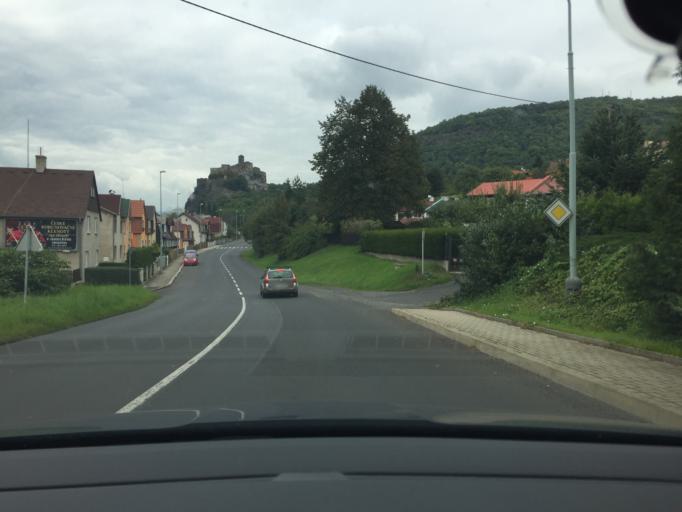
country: CZ
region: Ustecky
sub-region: Okres Usti nad Labem
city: Usti nad Labem
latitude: 50.6331
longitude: 14.0542
